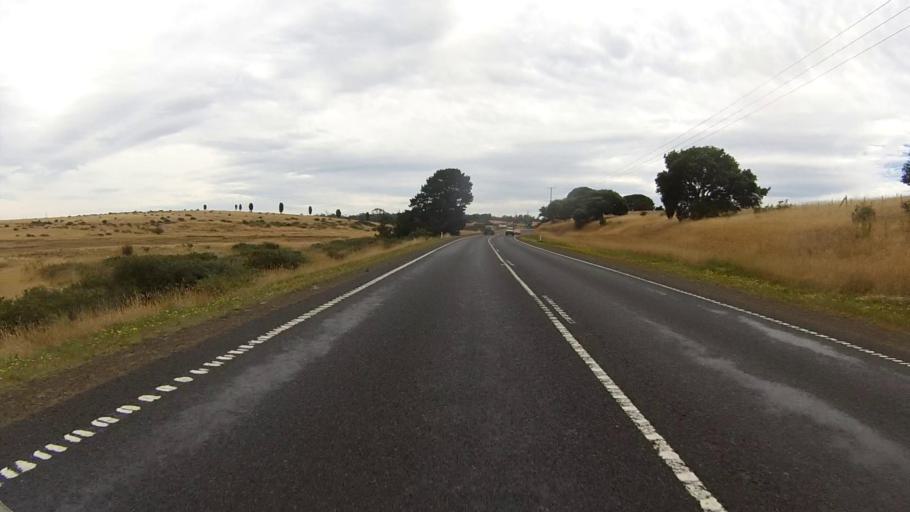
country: AU
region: Tasmania
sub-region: Northern Midlands
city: Evandale
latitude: -41.8458
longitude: 147.4489
